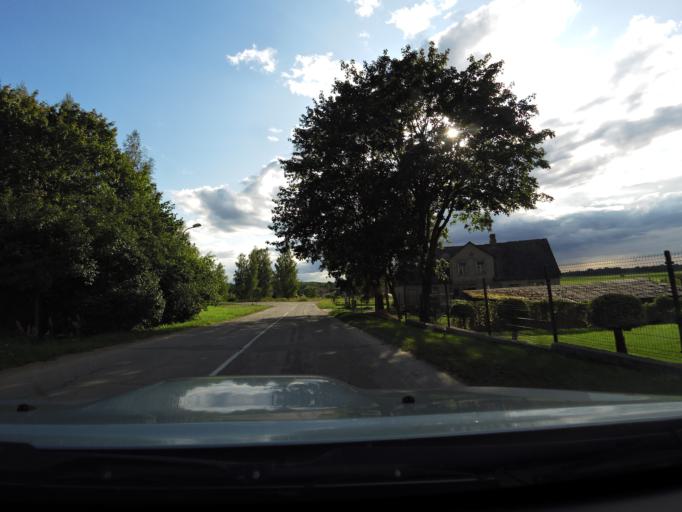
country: LV
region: Nereta
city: Nereta
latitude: 56.2099
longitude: 25.3021
